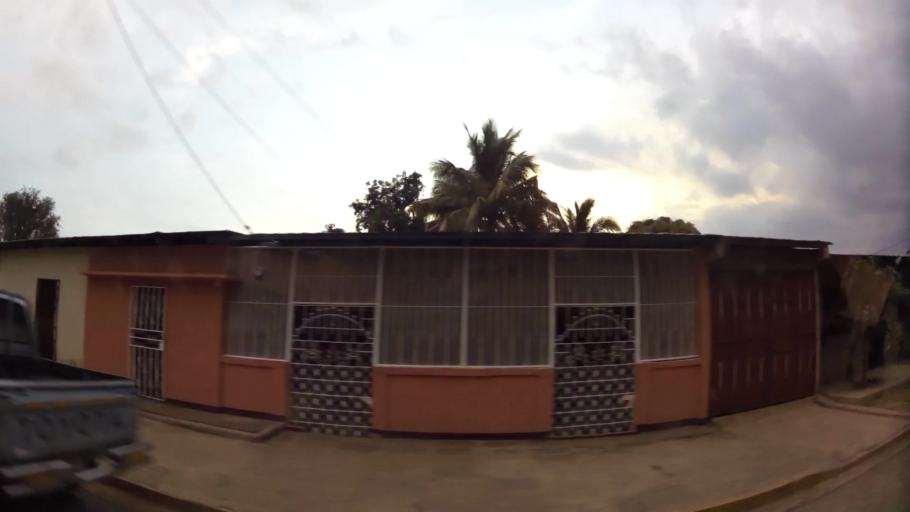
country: NI
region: Matagalpa
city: Ciudad Dario
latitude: 12.8546
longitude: -86.0944
